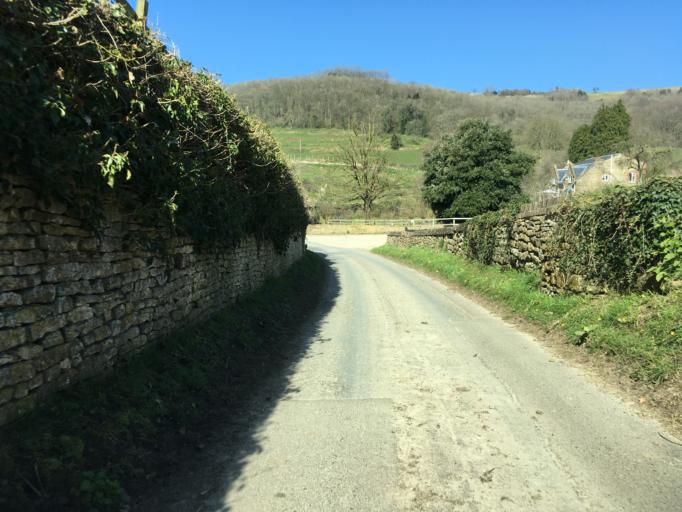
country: GB
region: England
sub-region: Gloucestershire
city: Dursley
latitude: 51.6761
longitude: -2.3775
